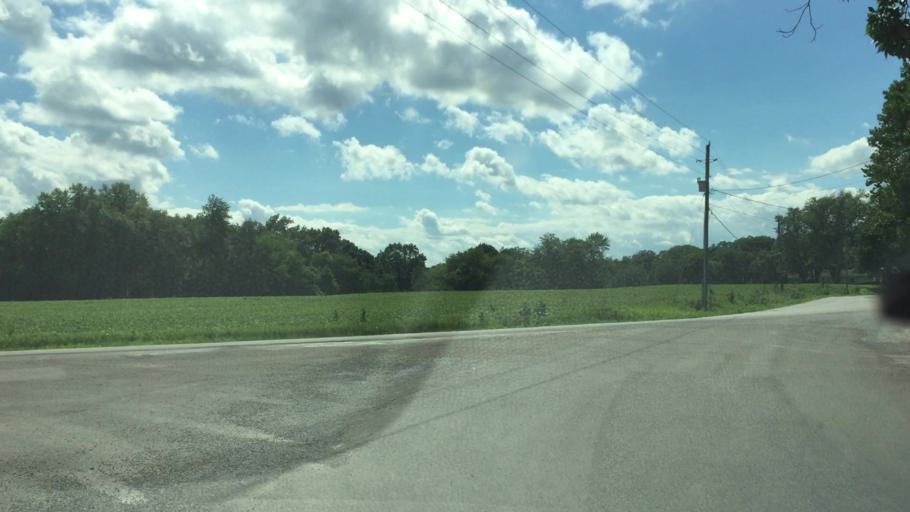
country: US
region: Iowa
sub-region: Linn County
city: Ely
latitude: 41.8273
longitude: -91.6230
